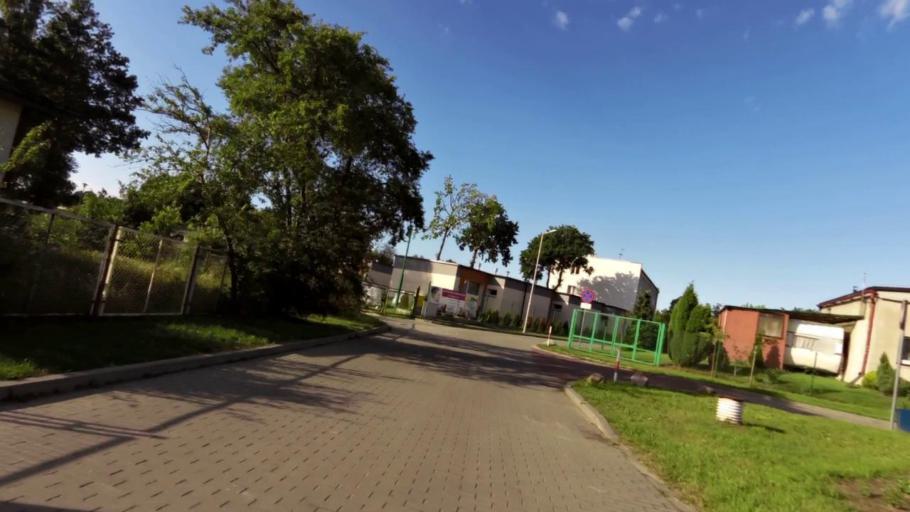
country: PL
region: West Pomeranian Voivodeship
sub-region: Powiat slawienski
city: Darlowo
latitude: 54.3796
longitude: 16.3169
